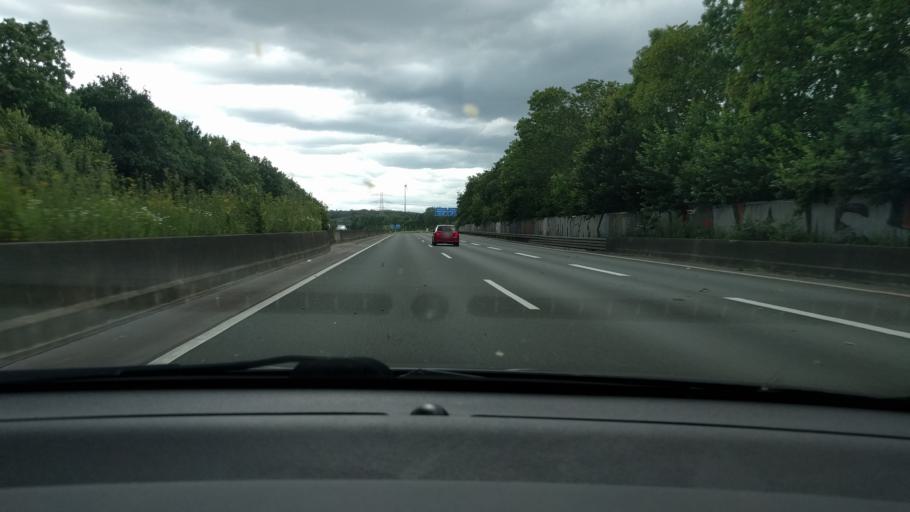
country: DE
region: North Rhine-Westphalia
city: Castrop-Rauxel
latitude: 51.5668
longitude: 7.3606
